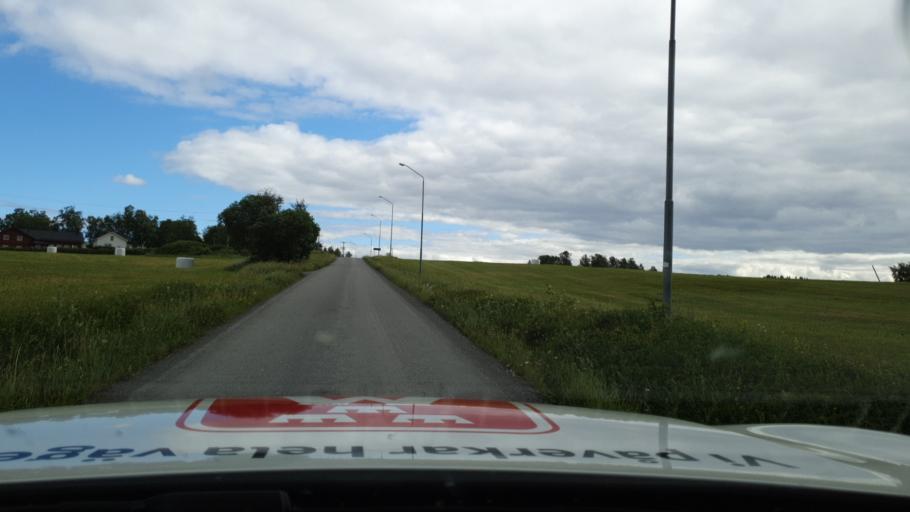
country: SE
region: Jaemtland
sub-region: OEstersunds Kommun
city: Ostersund
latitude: 63.1339
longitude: 14.5743
